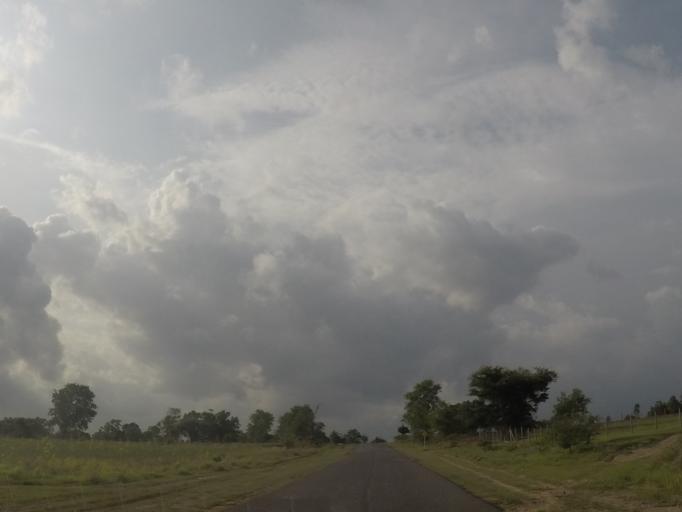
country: MM
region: Mandalay
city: Meiktila
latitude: 20.5247
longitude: 95.7025
